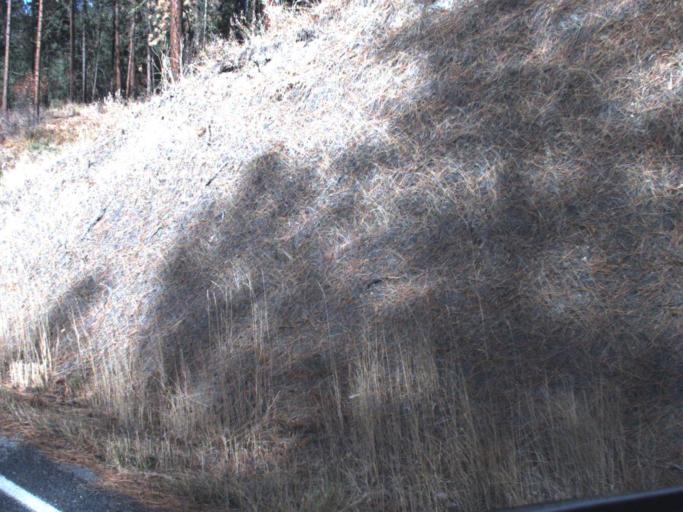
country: US
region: Washington
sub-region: Stevens County
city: Kettle Falls
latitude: 48.3468
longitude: -118.1611
